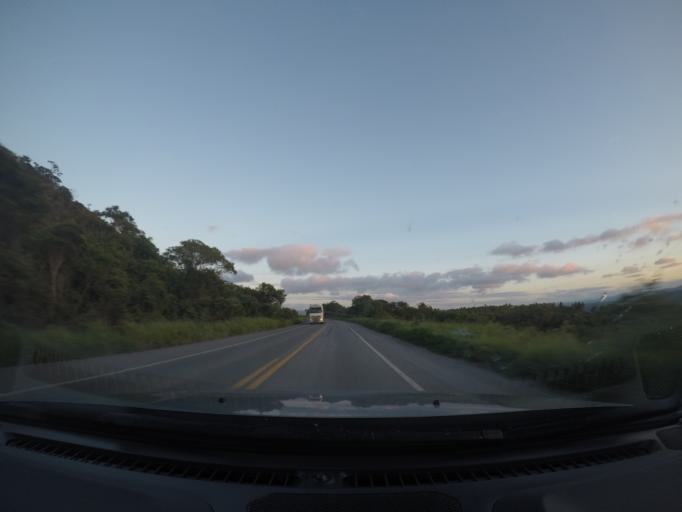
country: BR
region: Bahia
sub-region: Seabra
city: Seabra
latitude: -12.4323
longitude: -41.8244
